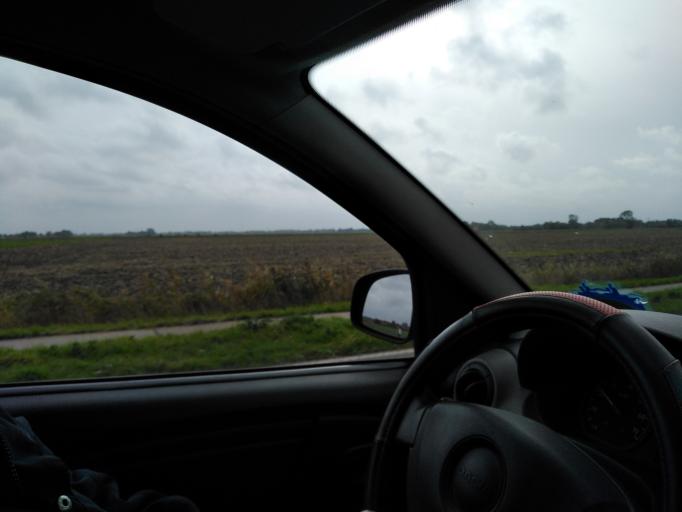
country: DE
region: Lower Saxony
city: Schillig
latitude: 53.6851
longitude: 7.9995
